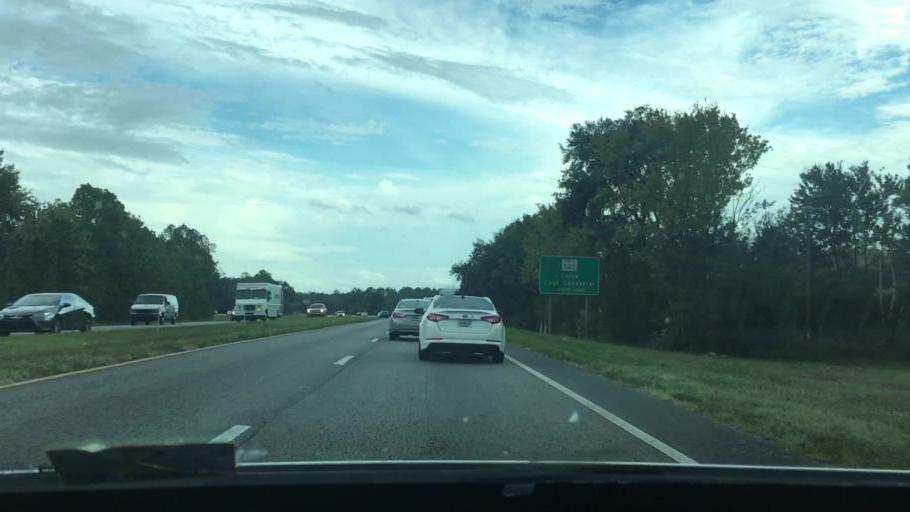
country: US
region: Florida
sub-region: Orange County
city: Bithlo
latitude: 28.5408
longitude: -81.0852
